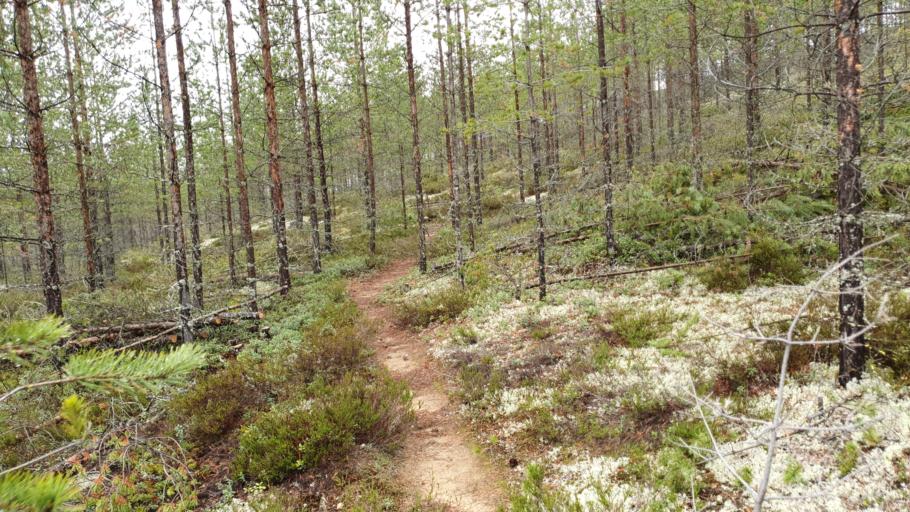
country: FI
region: Kainuu
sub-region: Kehys-Kainuu
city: Kuhmo
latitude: 64.1503
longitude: 29.4002
